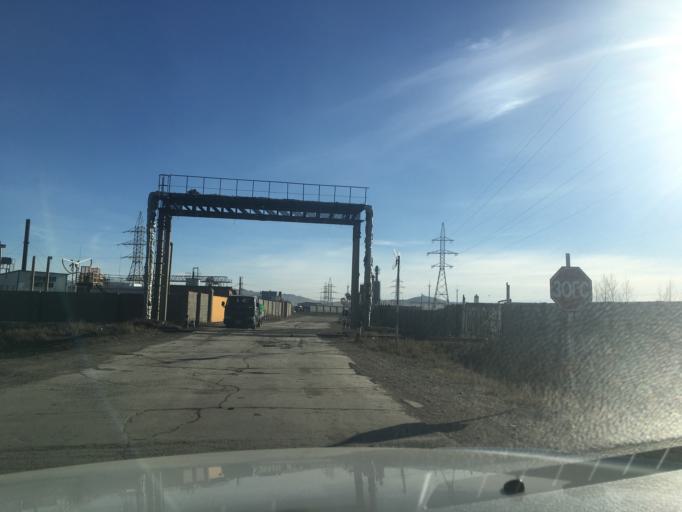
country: MN
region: Ulaanbaatar
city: Ulaanbaatar
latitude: 47.9008
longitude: 106.7352
